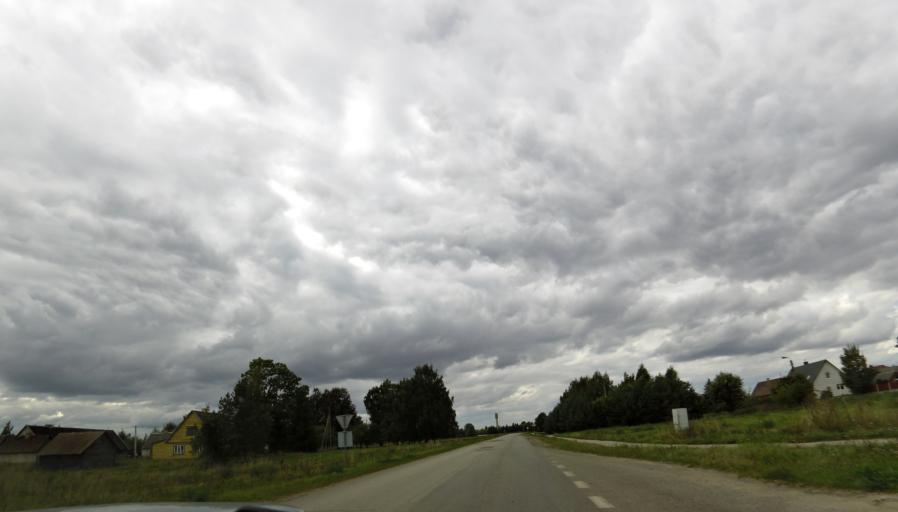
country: LT
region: Panevezys
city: Pasvalys
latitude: 56.0790
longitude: 24.3697
